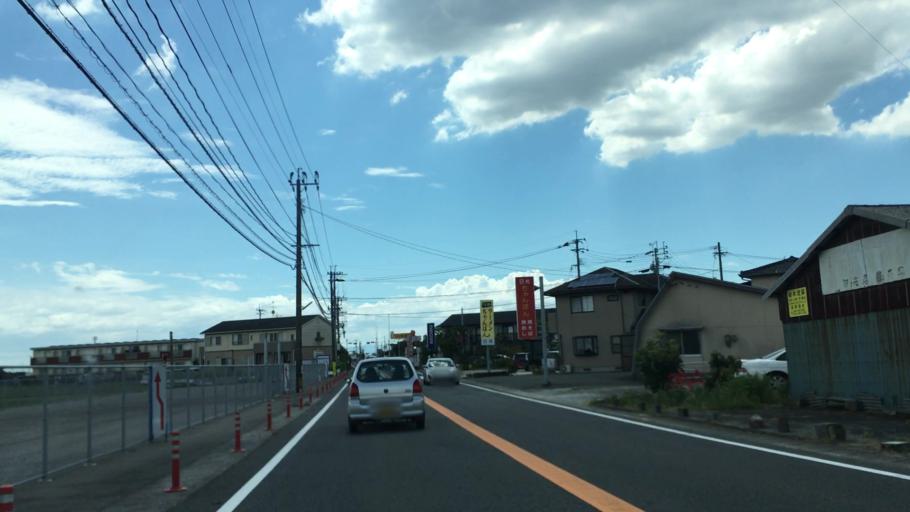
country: JP
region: Saga Prefecture
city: Kanzakimachi-kanzaki
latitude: 33.2883
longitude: 130.3515
